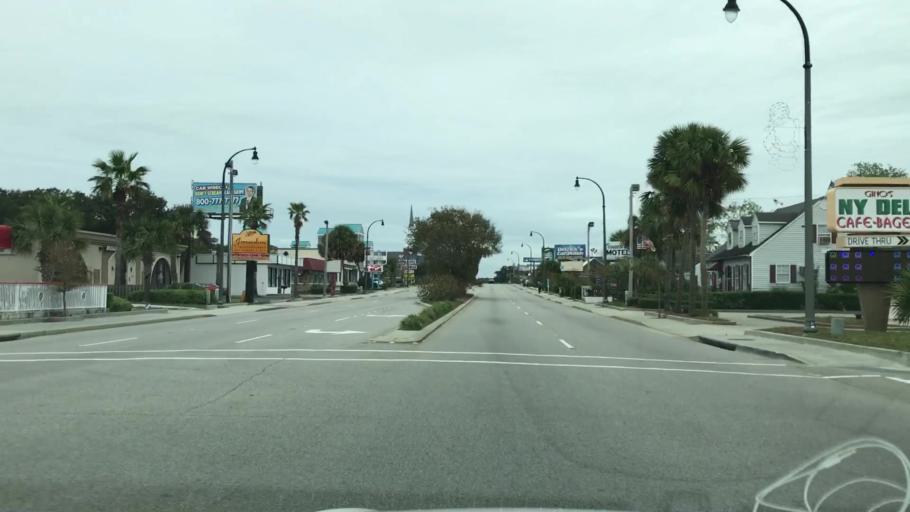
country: US
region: South Carolina
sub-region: Horry County
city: Myrtle Beach
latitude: 33.6866
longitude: -78.8897
